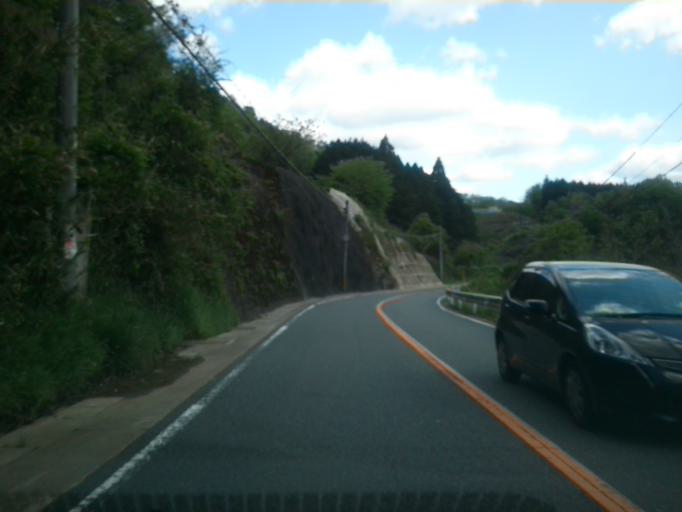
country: JP
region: Kyoto
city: Fukuchiyama
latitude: 35.3447
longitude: 135.0661
